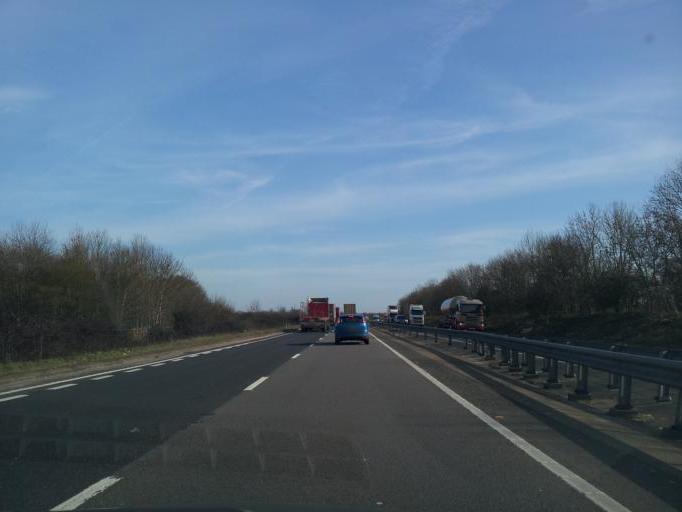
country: GB
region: England
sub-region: Bedford
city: Pertenhall
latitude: 52.3432
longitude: -0.3413
